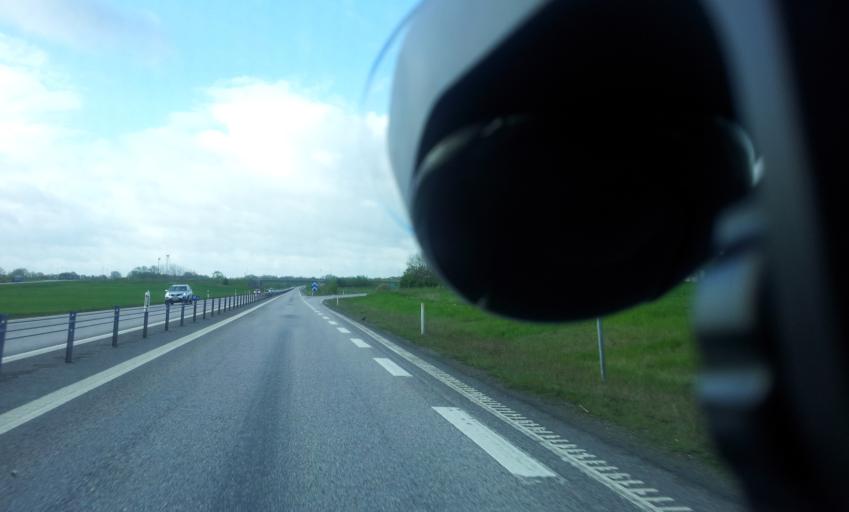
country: SE
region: Kalmar
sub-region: Torsas Kommun
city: Torsas
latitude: 56.4564
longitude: 16.0785
